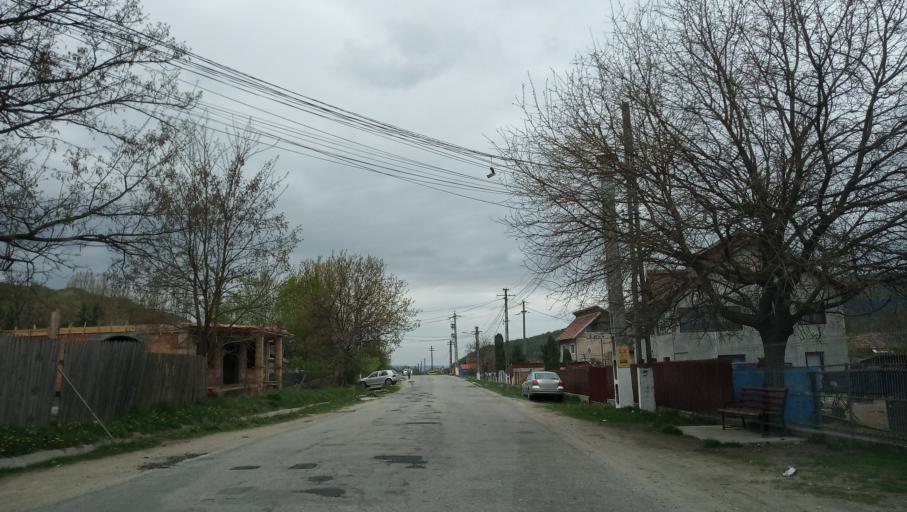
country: RO
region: Valcea
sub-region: Comuna Daesti
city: Daesti
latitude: 45.1746
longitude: 24.3771
